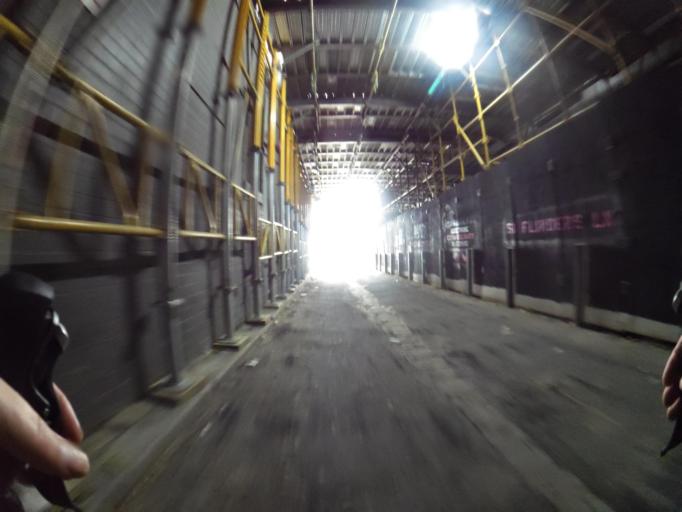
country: AU
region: Victoria
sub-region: Melbourne
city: Melbourne
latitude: -37.8162
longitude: 144.9732
